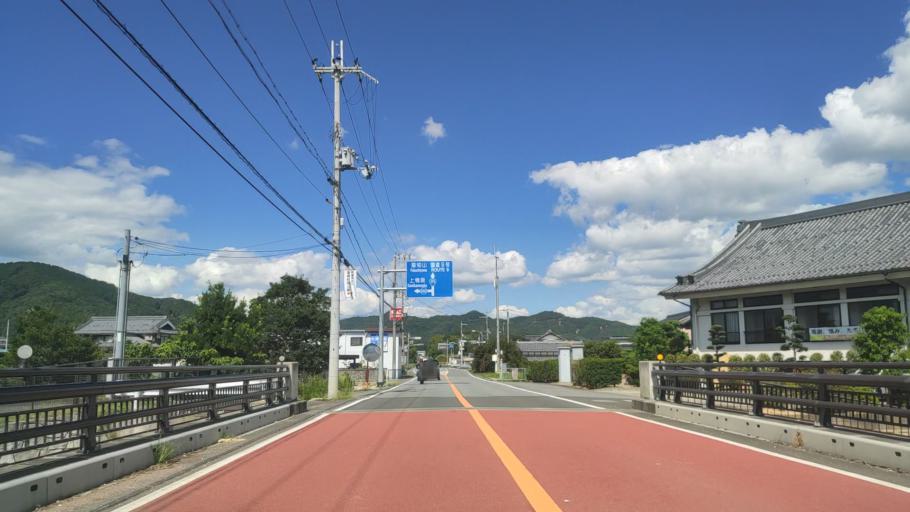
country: JP
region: Kyoto
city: Fukuchiyama
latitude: 35.2260
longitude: 135.1296
